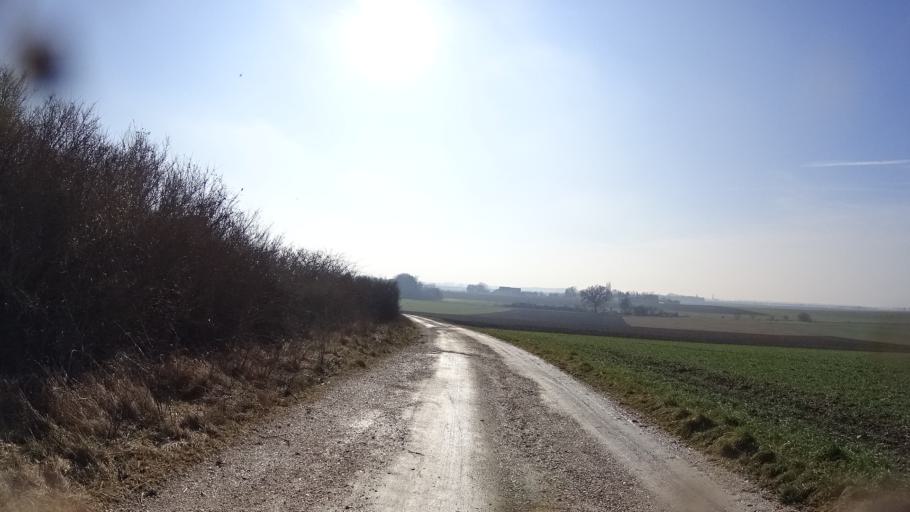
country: DE
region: Bavaria
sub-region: Upper Bavaria
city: Wettstetten
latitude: 48.8335
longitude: 11.3883
